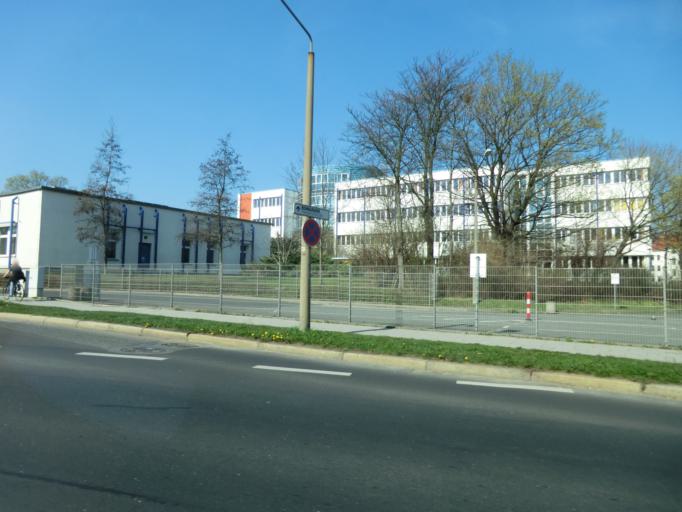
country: DE
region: Saxony
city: Goerlitz
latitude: 51.1536
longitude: 14.9708
